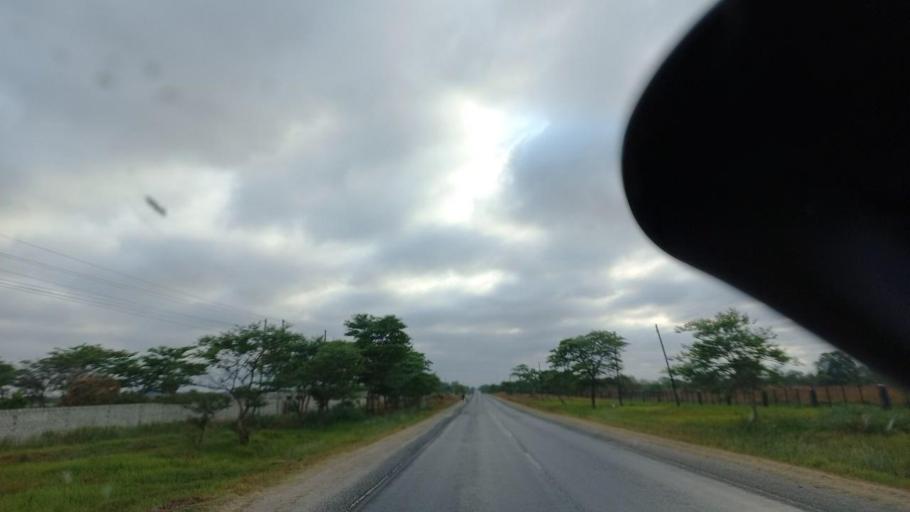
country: ZM
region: Lusaka
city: Chongwe
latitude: -15.3520
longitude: 28.4914
